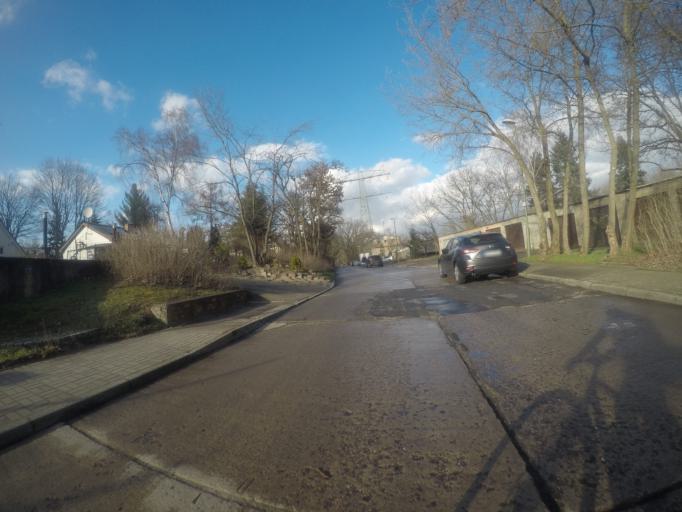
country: DE
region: Berlin
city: Karlshorst
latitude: 52.4962
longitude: 13.5402
